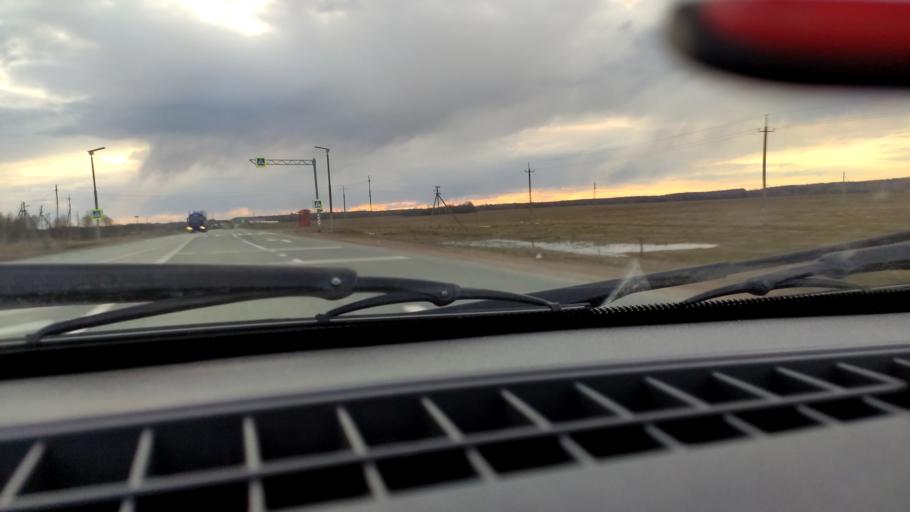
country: RU
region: Bashkortostan
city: Kudeyevskiy
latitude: 54.8169
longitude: 56.7559
